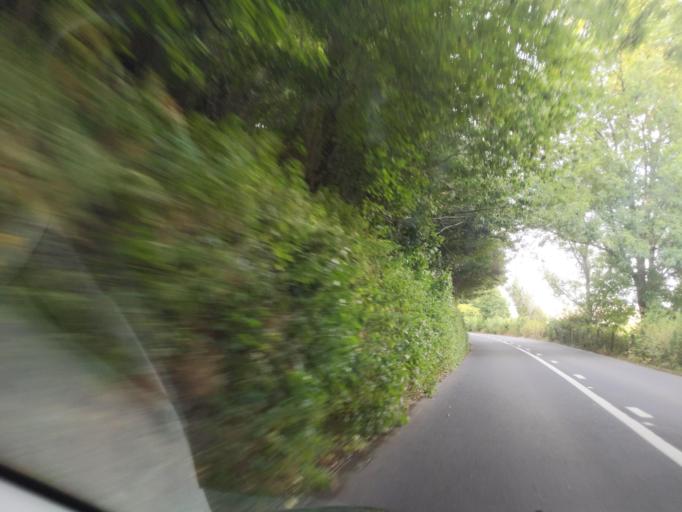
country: GB
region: England
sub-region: Devon
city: Winkleigh
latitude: 50.9643
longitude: -3.9649
